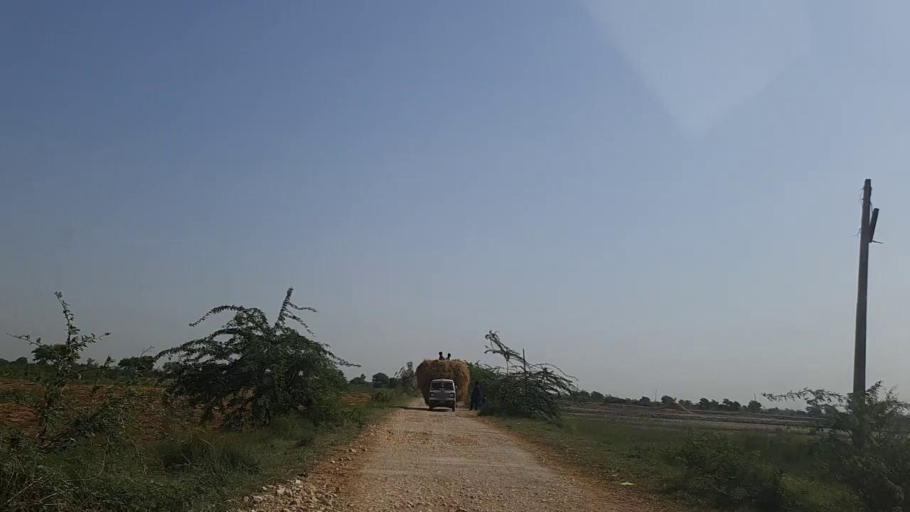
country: PK
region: Sindh
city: Daro Mehar
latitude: 24.7208
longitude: 68.0951
